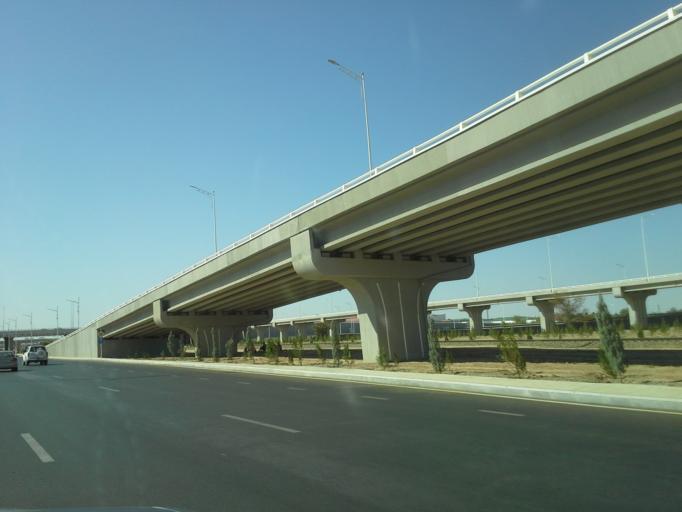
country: TM
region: Ahal
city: Ashgabat
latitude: 37.9259
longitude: 58.4316
